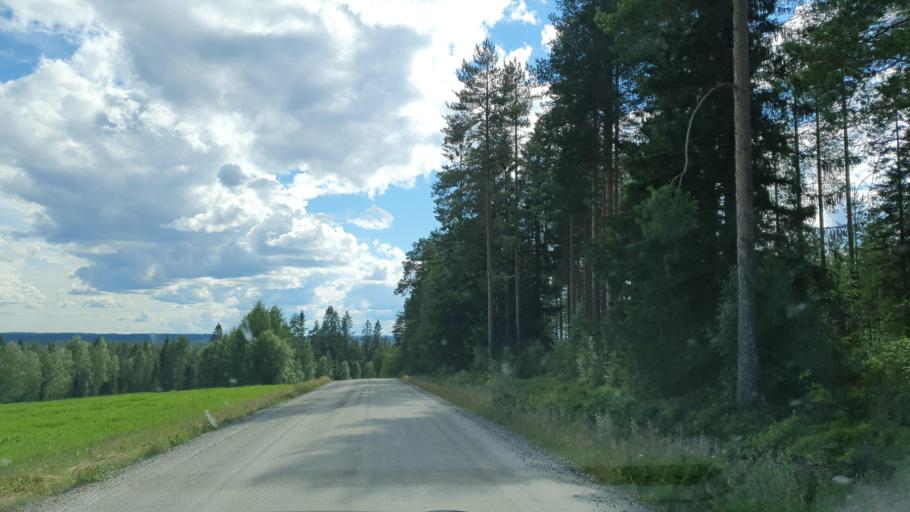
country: FI
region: Kainuu
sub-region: Kehys-Kainuu
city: Kuhmo
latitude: 64.1271
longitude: 29.6431
